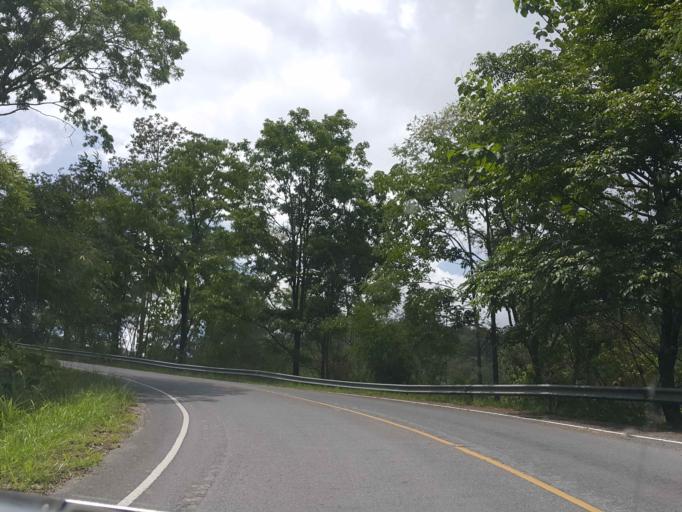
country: TH
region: Chiang Mai
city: Samoeng
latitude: 18.8216
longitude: 98.7874
